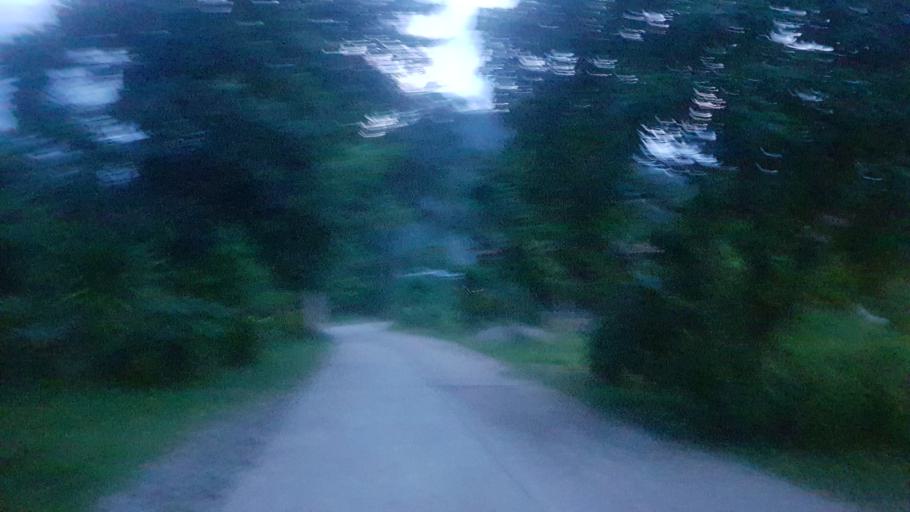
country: TH
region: Phangnga
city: Takua Pa
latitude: 8.9113
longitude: 98.5276
